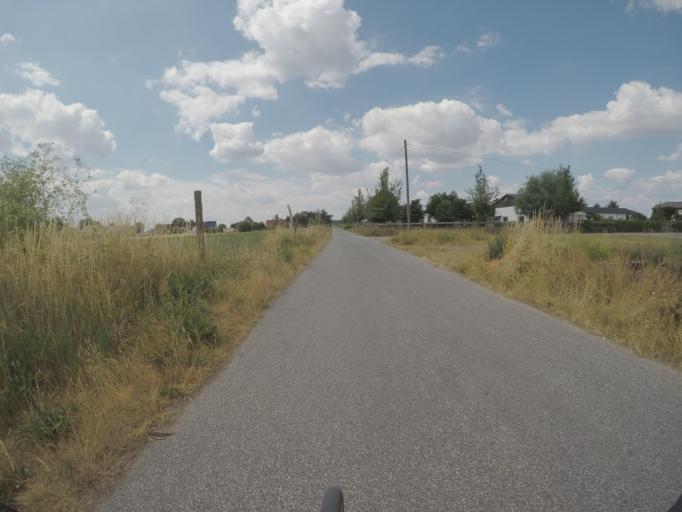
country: DE
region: Brandenburg
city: Roskow
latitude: 52.4460
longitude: 12.6630
